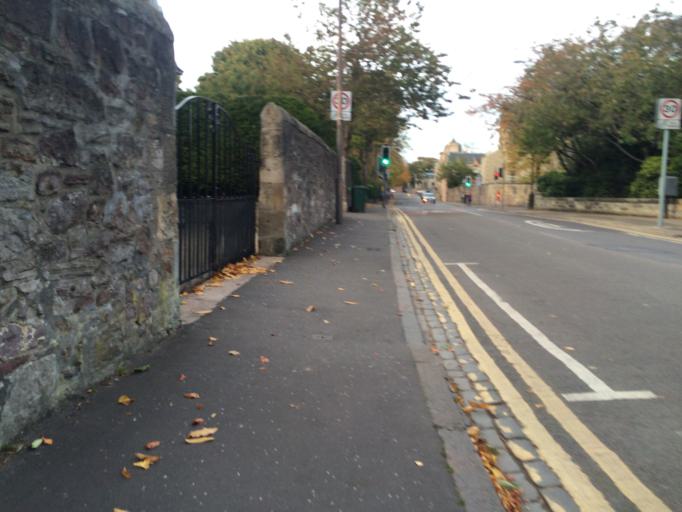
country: GB
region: Scotland
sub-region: Edinburgh
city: Edinburgh
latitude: 55.9331
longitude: -3.2007
